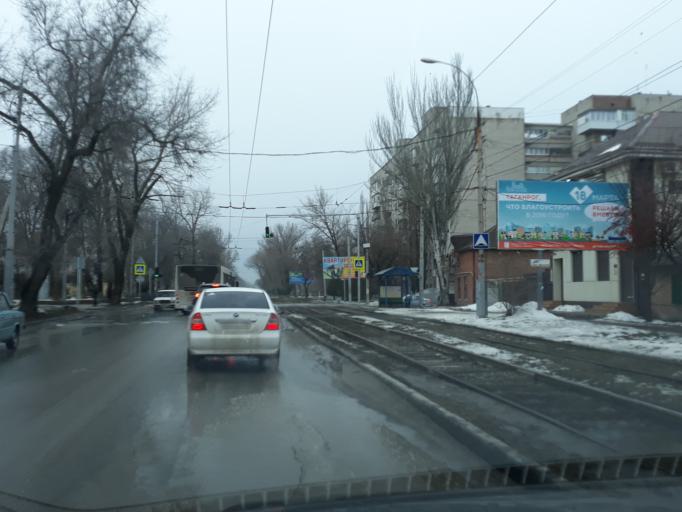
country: RU
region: Rostov
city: Taganrog
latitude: 47.2359
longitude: 38.9170
